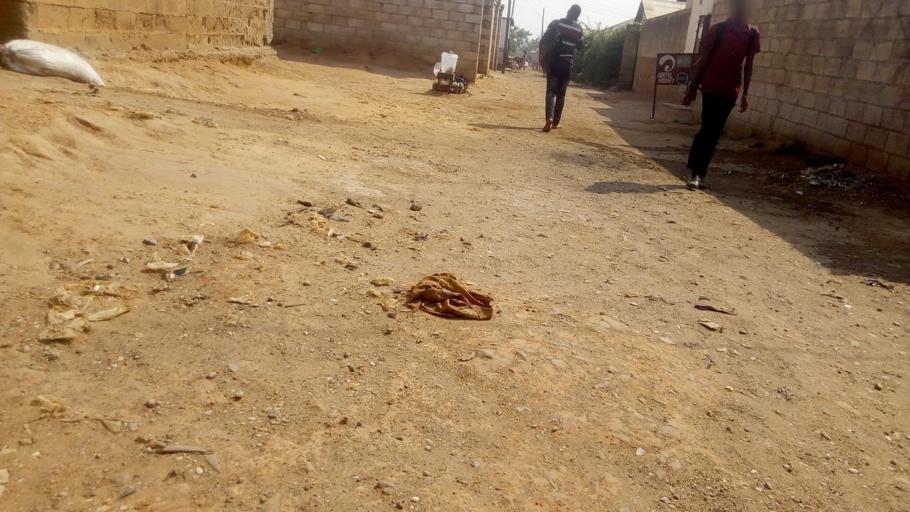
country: ZM
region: Lusaka
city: Lusaka
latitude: -15.3594
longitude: 28.2856
